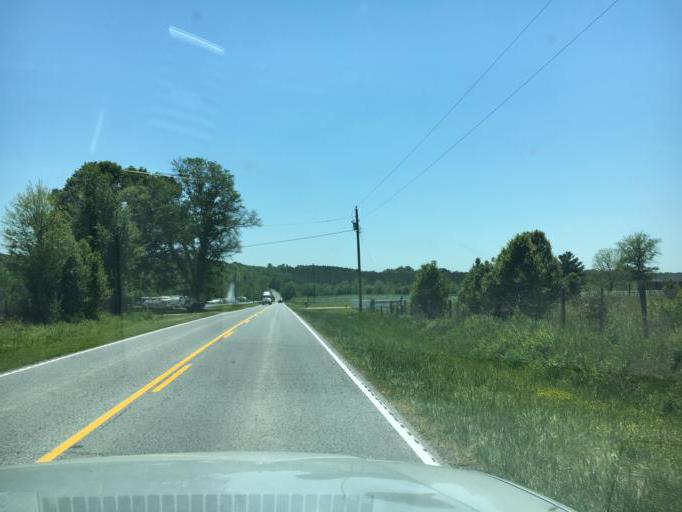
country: US
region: South Carolina
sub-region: Cherokee County
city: Blacksburg
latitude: 35.1634
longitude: -81.5747
